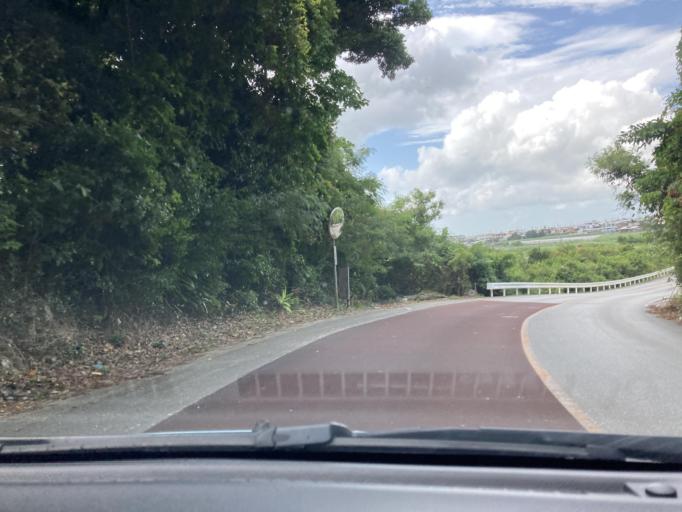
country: JP
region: Okinawa
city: Itoman
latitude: 26.0983
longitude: 127.6989
